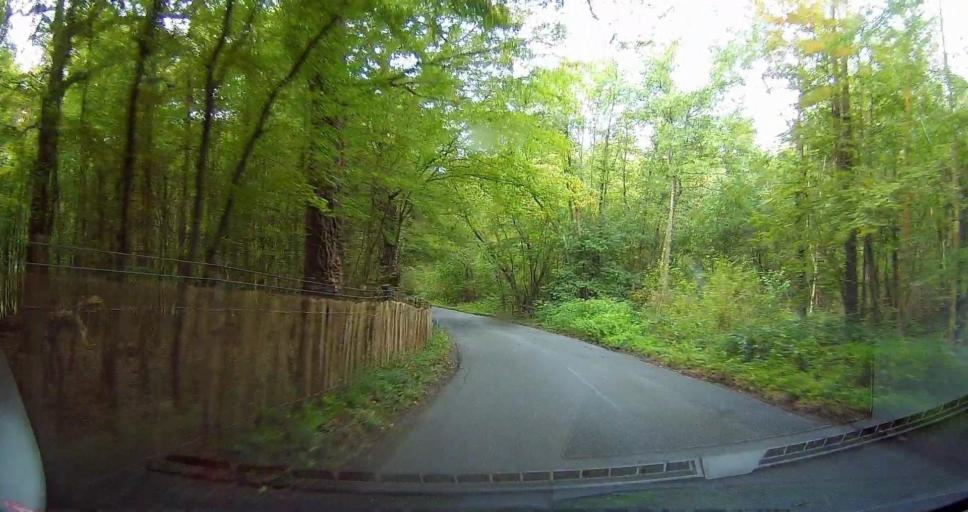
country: GB
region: England
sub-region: Kent
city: Hadlow
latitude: 51.2342
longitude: 0.2979
